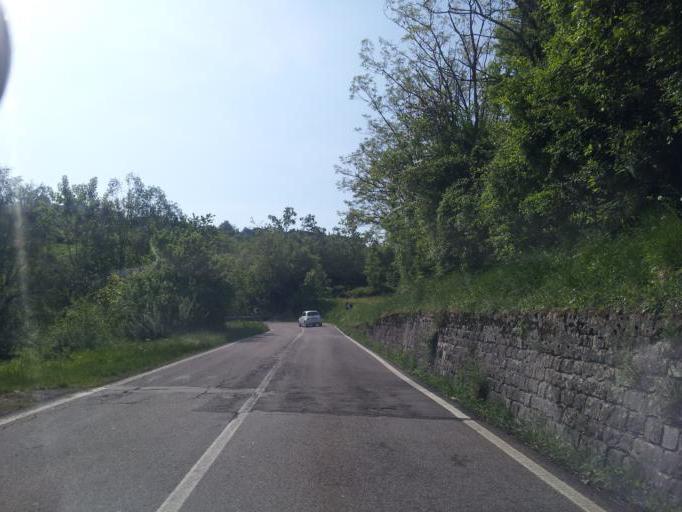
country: IT
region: Emilia-Romagna
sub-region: Provincia di Reggio Emilia
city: Villa Minozzo
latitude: 44.3689
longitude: 10.4619
